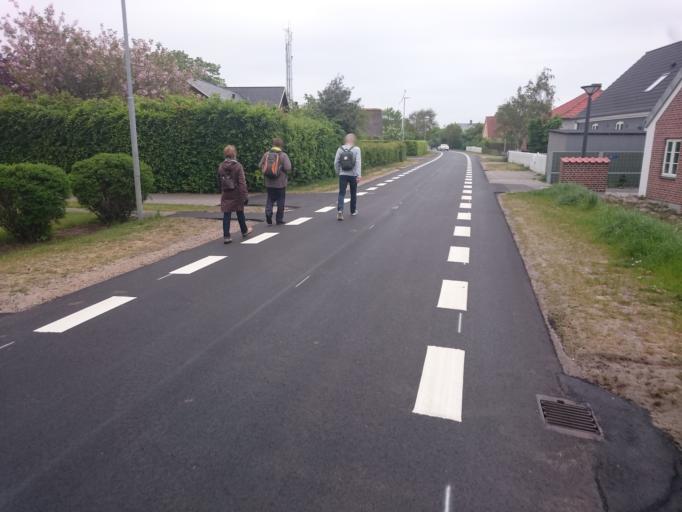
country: DK
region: South Denmark
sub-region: Fano Kommune
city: Nordby
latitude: 55.4429
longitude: 8.3985
